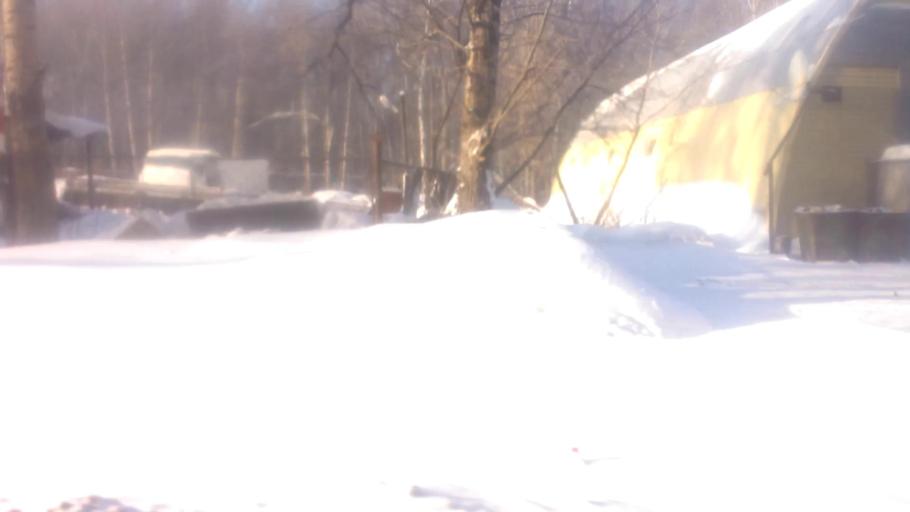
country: RU
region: Altai Krai
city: Novosilikatnyy
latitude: 53.3730
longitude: 83.6625
